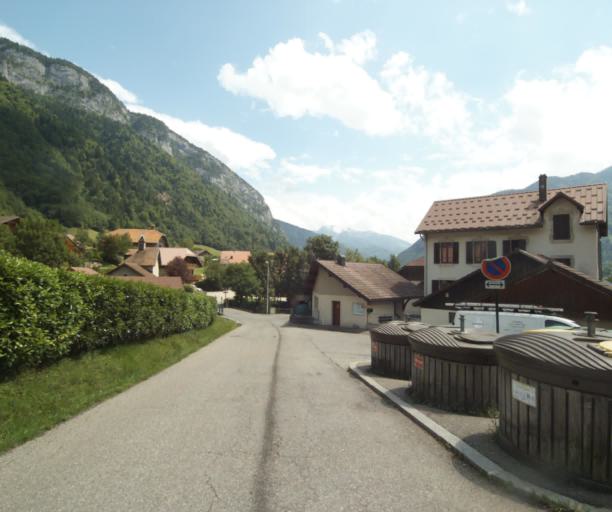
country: FR
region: Rhone-Alpes
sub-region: Departement de la Haute-Savoie
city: Thones
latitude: 45.8982
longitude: 6.3024
